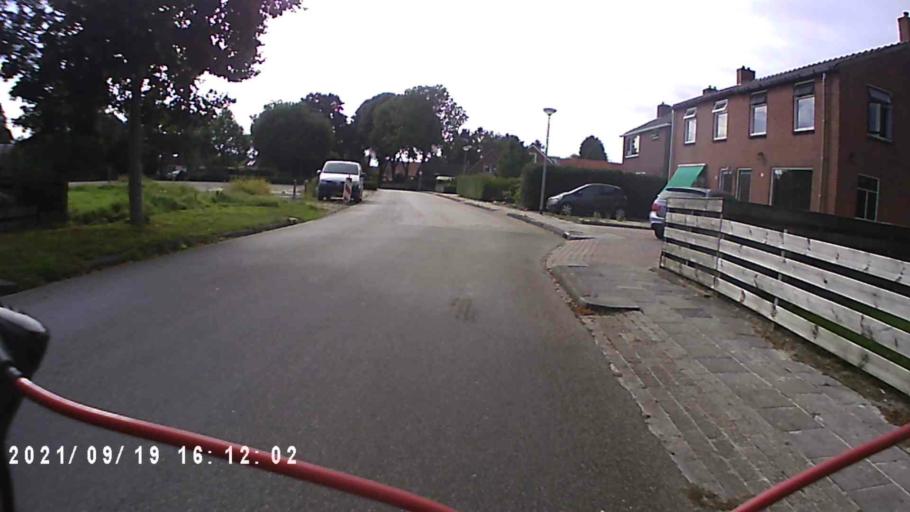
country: DE
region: Lower Saxony
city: Bunde
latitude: 53.1815
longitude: 7.2118
